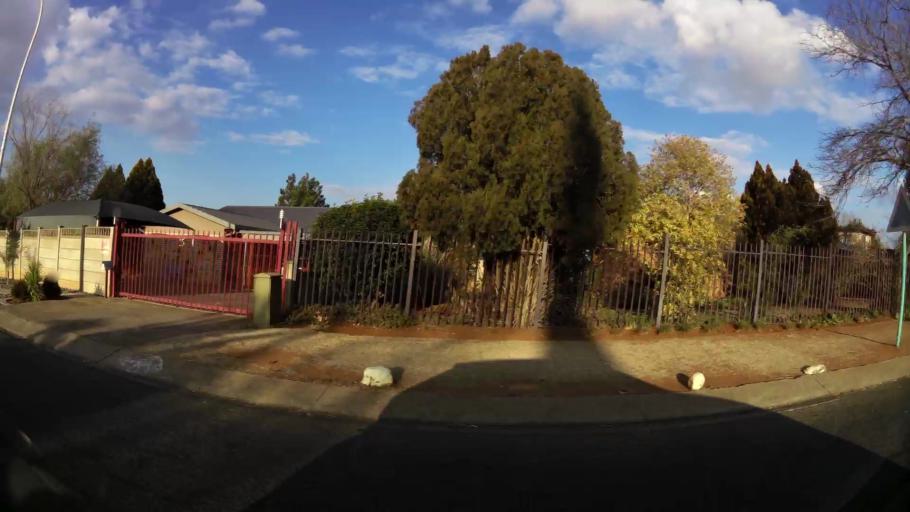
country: ZA
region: Orange Free State
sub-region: Mangaung Metropolitan Municipality
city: Bloemfontein
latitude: -29.1507
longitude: 26.1860
